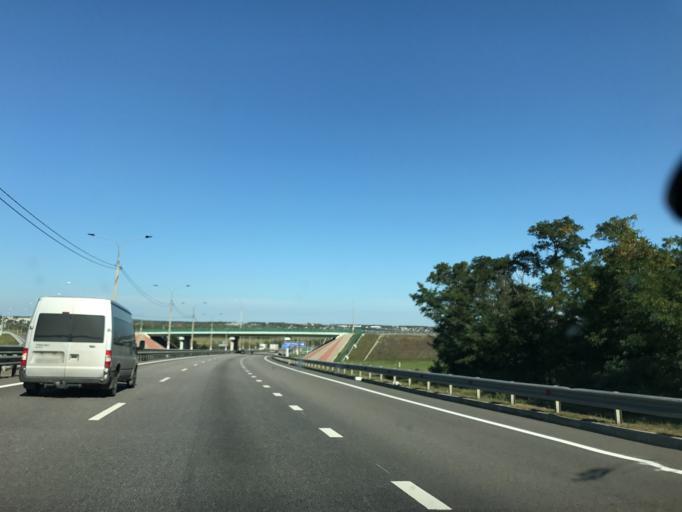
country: RU
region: Voronezj
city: Verkhniy Mamon
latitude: 50.1491
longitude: 40.4280
